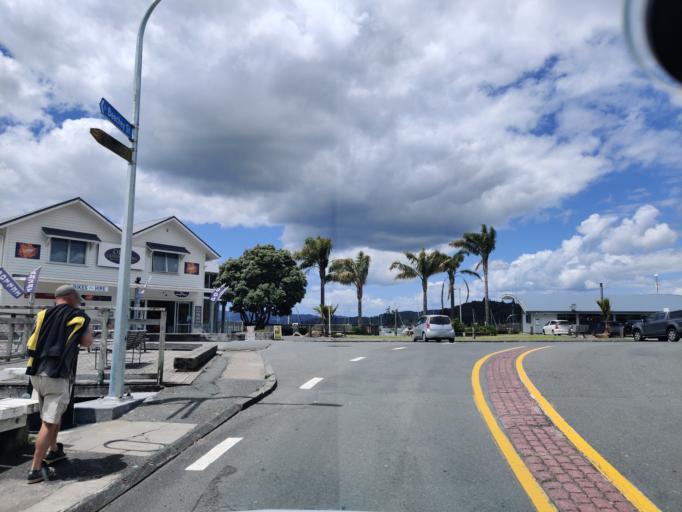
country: NZ
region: Northland
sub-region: Far North District
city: Paihia
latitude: -35.3125
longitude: 174.1211
